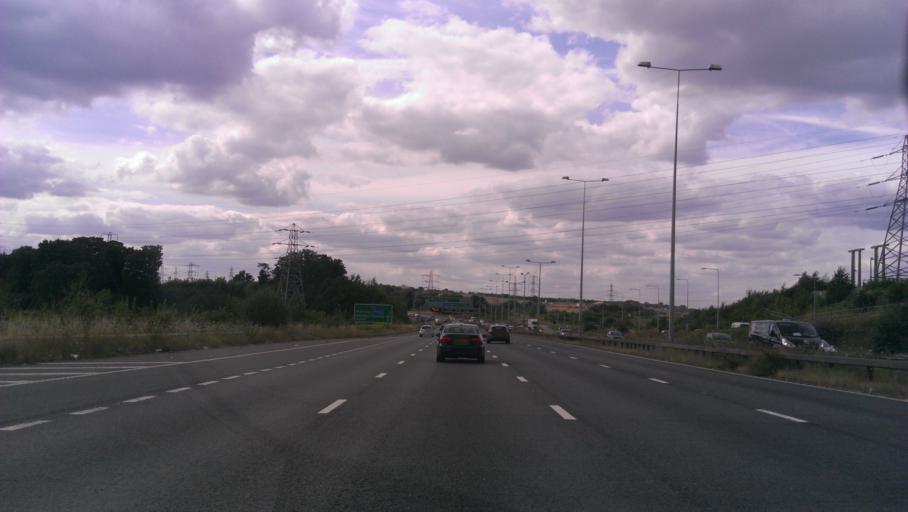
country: GB
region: England
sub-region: Kent
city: Swanscombe
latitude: 51.4268
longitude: 0.3298
